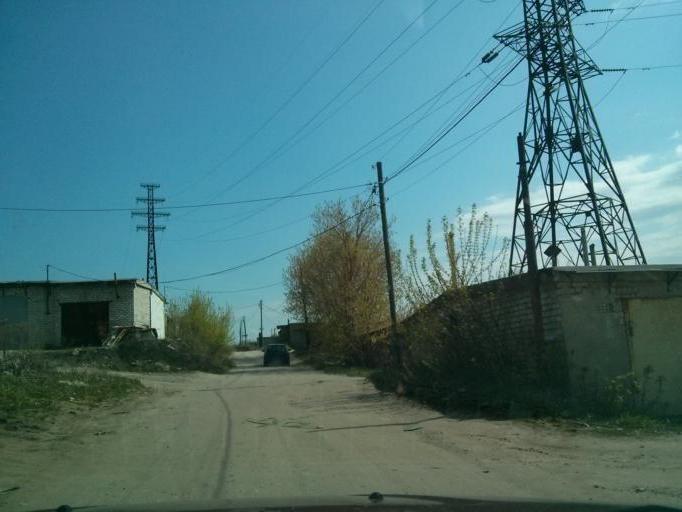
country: RU
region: Vladimir
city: Murom
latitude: 55.5638
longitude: 42.0700
